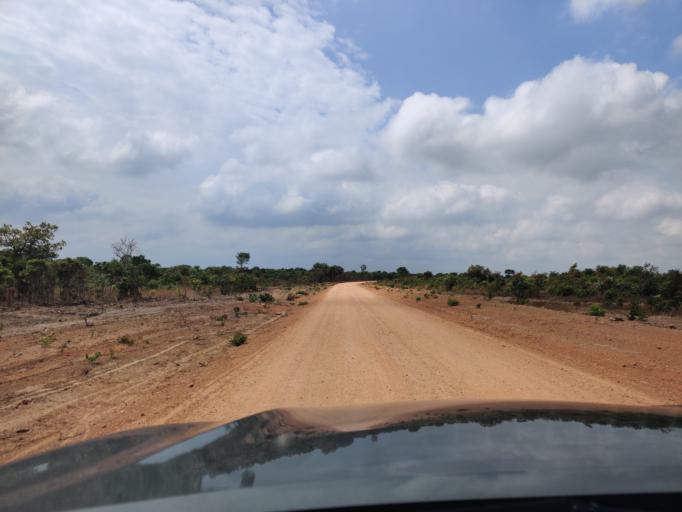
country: ZM
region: Central
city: Mkushi
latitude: -13.6588
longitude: 29.7520
